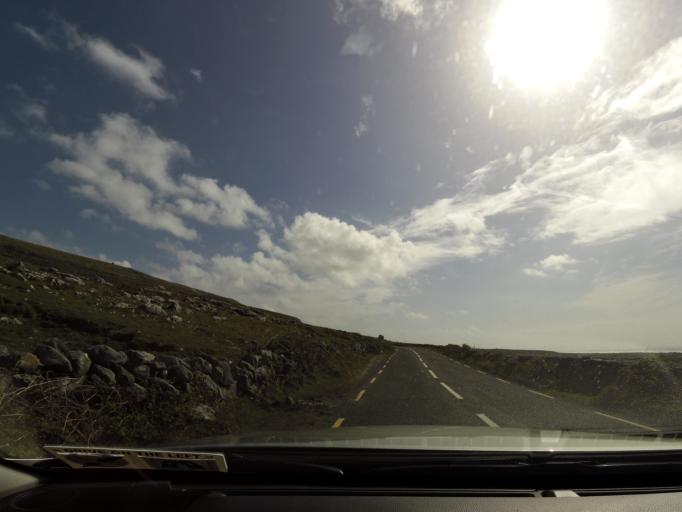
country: IE
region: Connaught
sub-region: County Galway
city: Bearna
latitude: 53.1483
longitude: -9.2705
